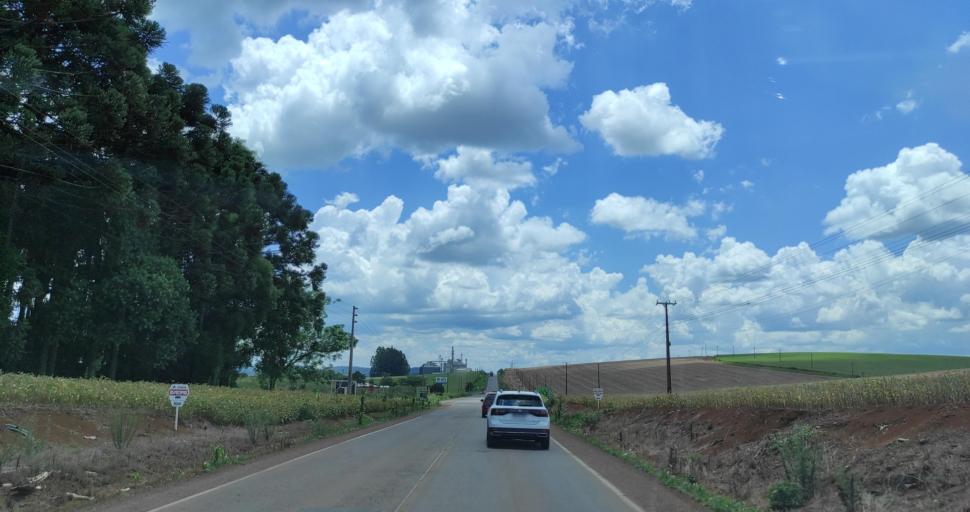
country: BR
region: Santa Catarina
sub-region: Xanxere
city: Xanxere
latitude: -26.7705
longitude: -52.4058
